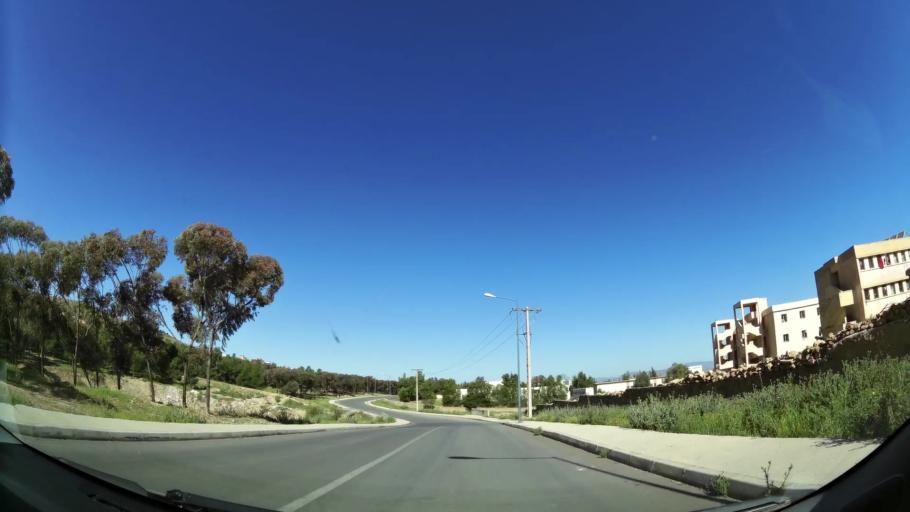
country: MA
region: Oriental
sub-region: Oujda-Angad
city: Oujda
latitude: 34.6480
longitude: -1.8983
